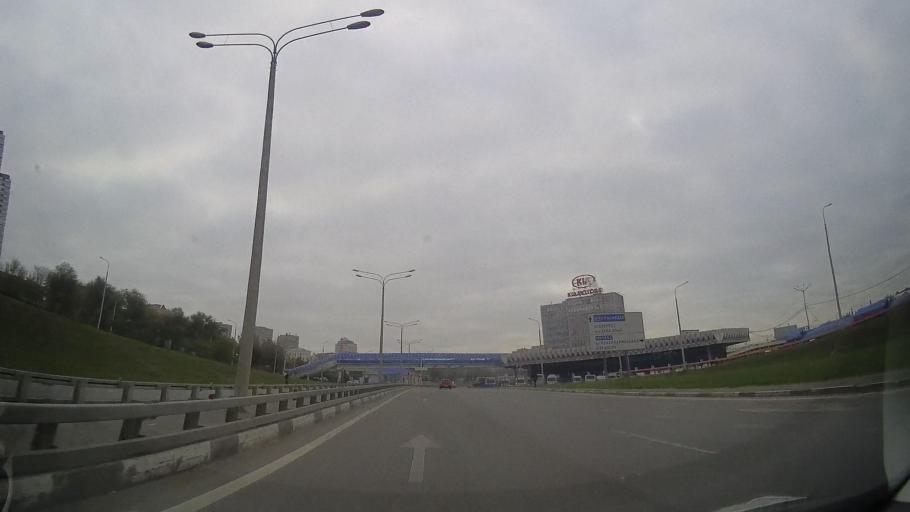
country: RU
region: Rostov
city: Rostov-na-Donu
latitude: 47.2218
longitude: 39.6924
